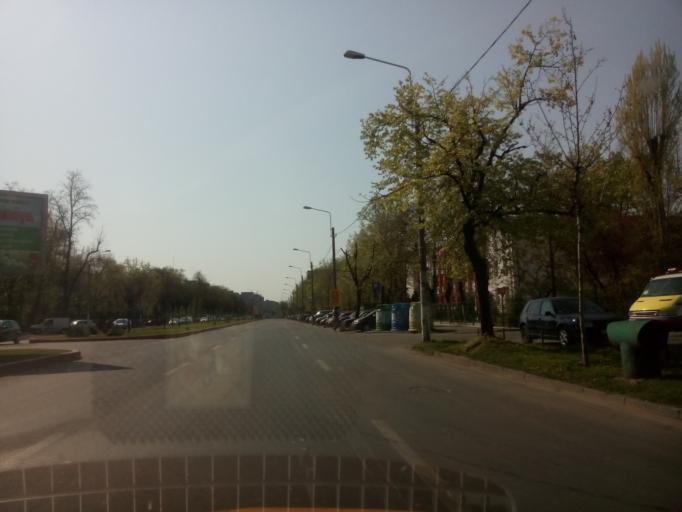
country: RO
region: Ilfov
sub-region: Comuna Fundeni-Dobroesti
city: Fundeni
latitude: 44.4330
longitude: 26.1607
